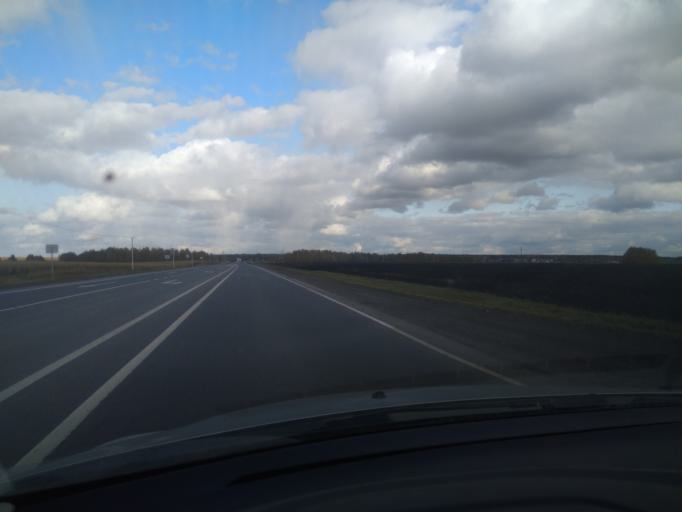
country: RU
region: Sverdlovsk
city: Zavodouspenskoye
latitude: 57.0862
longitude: 65.0249
